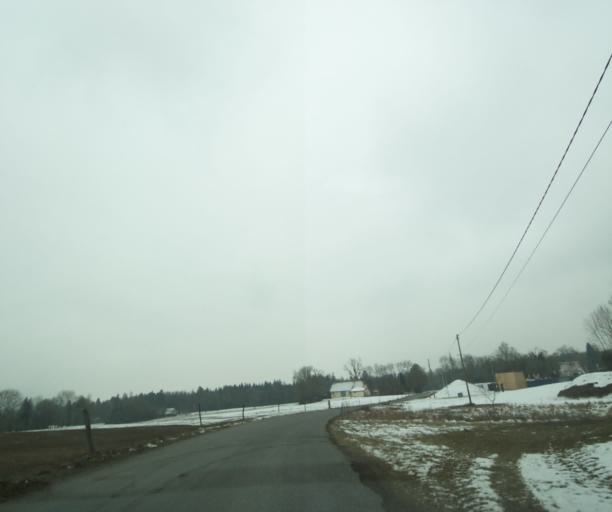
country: FR
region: Rhone-Alpes
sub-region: Departement de la Haute-Savoie
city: Reignier-Esery
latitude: 46.1222
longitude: 6.2890
